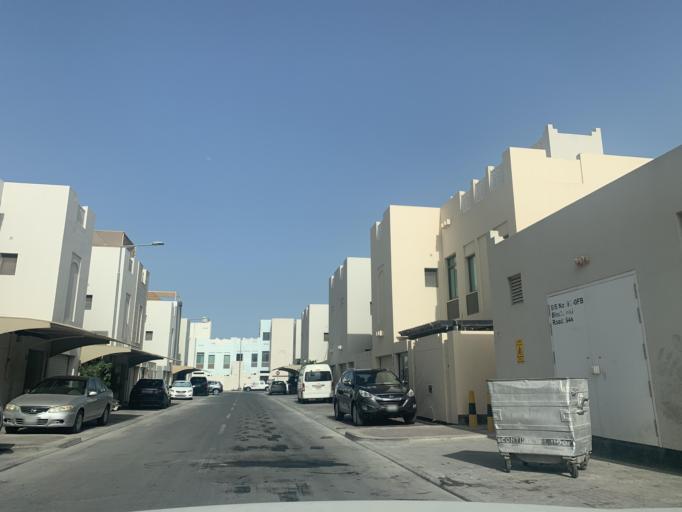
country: BH
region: Northern
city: Sitrah
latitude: 26.1599
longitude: 50.6268
